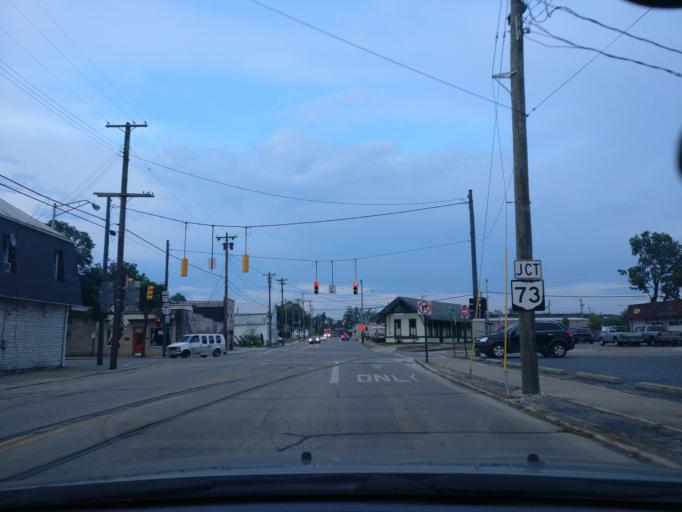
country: US
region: Ohio
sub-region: Warren County
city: Franklin
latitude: 39.5578
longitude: -84.3063
